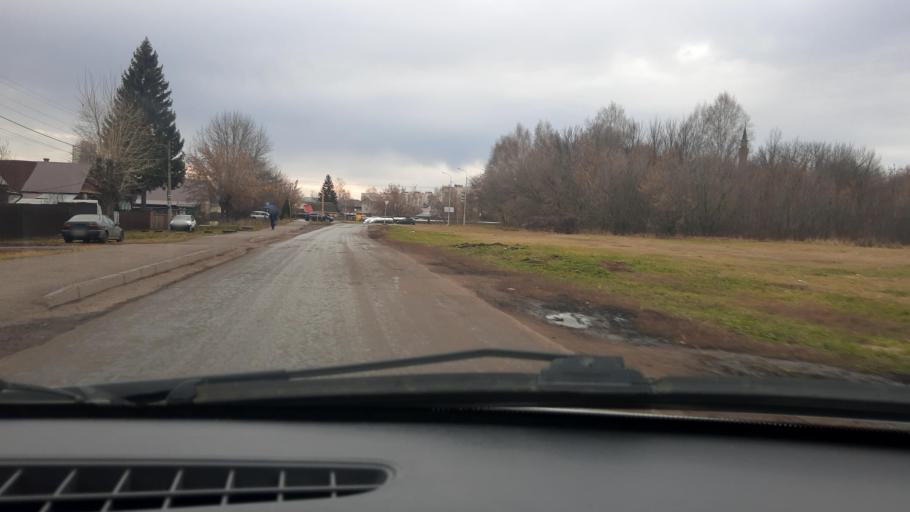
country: RU
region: Bashkortostan
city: Avdon
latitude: 54.7035
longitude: 55.8182
